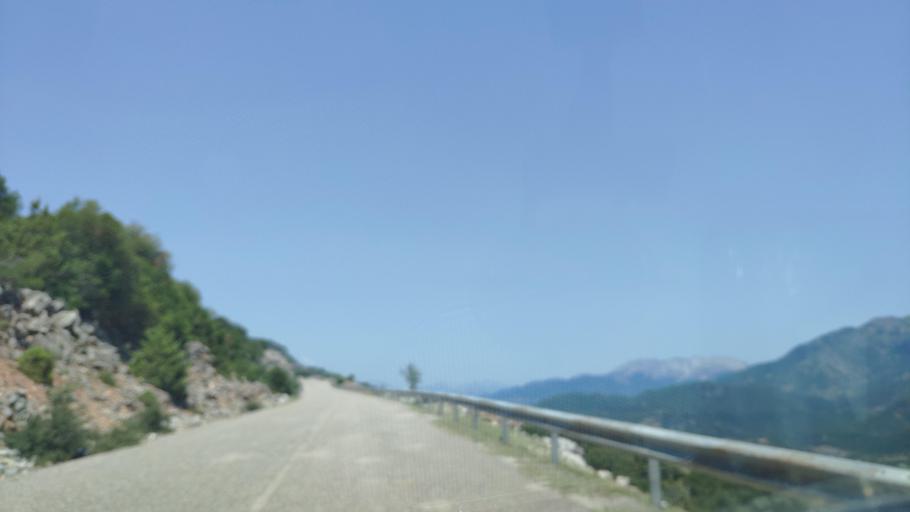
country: GR
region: Thessaly
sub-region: Nomos Kardhitsas
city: Anthiro
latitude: 39.1307
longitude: 21.3945
